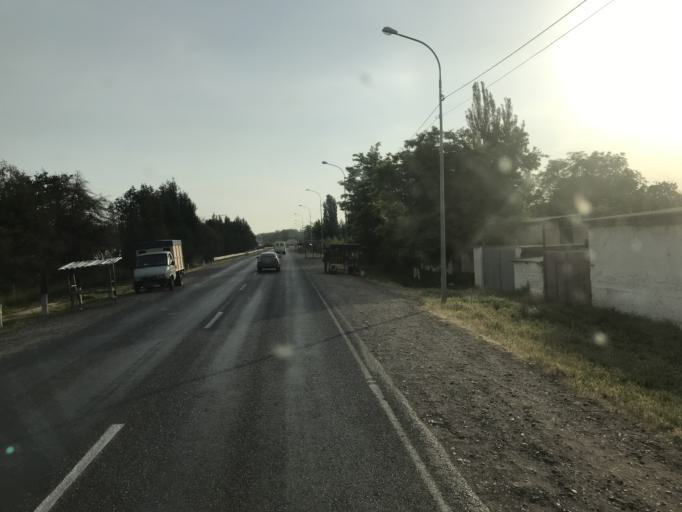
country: KZ
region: Ongtustik Qazaqstan
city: Saryaghash
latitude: 41.4872
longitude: 69.2572
